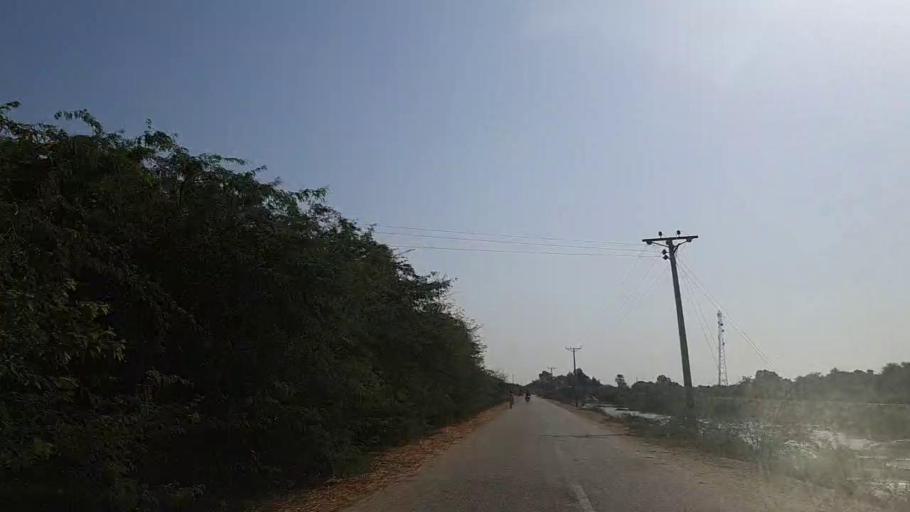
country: PK
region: Sindh
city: Jati
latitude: 24.5187
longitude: 68.2758
